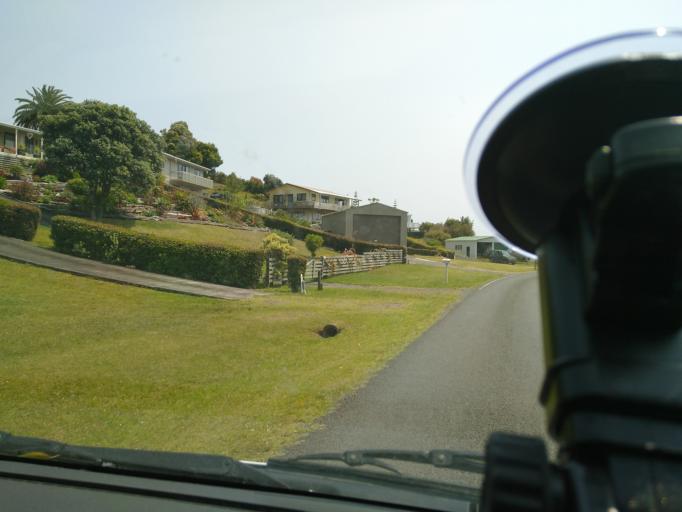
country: NZ
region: Northland
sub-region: Far North District
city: Kaitaia
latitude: -34.8163
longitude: 173.1164
